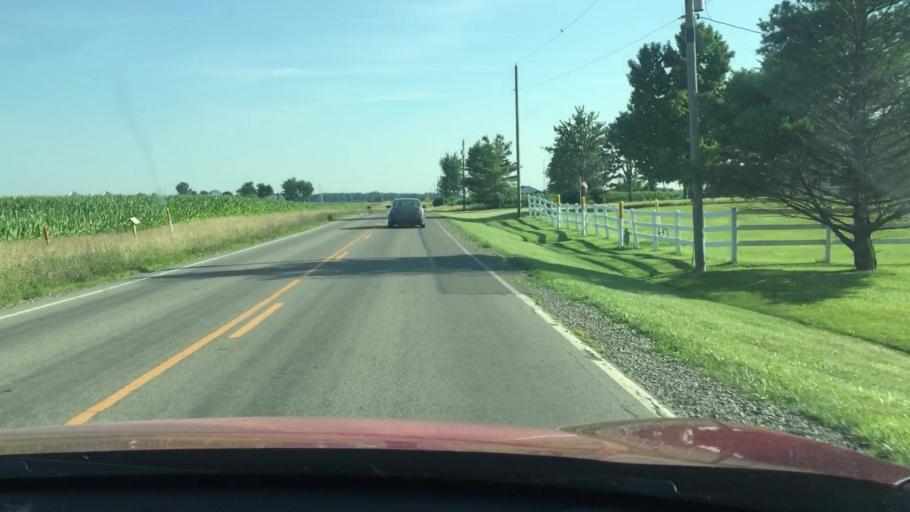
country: US
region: Ohio
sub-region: Hardin County
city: Ada
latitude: 40.6977
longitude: -83.8544
